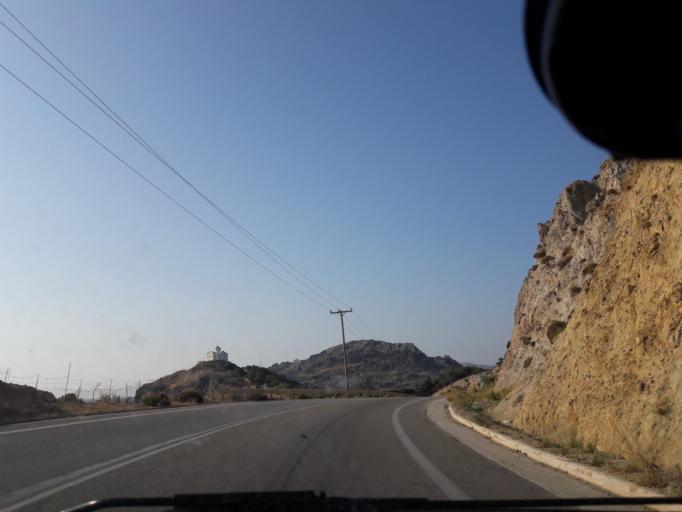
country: GR
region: North Aegean
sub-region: Nomos Lesvou
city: Myrina
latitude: 39.8663
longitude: 25.0554
